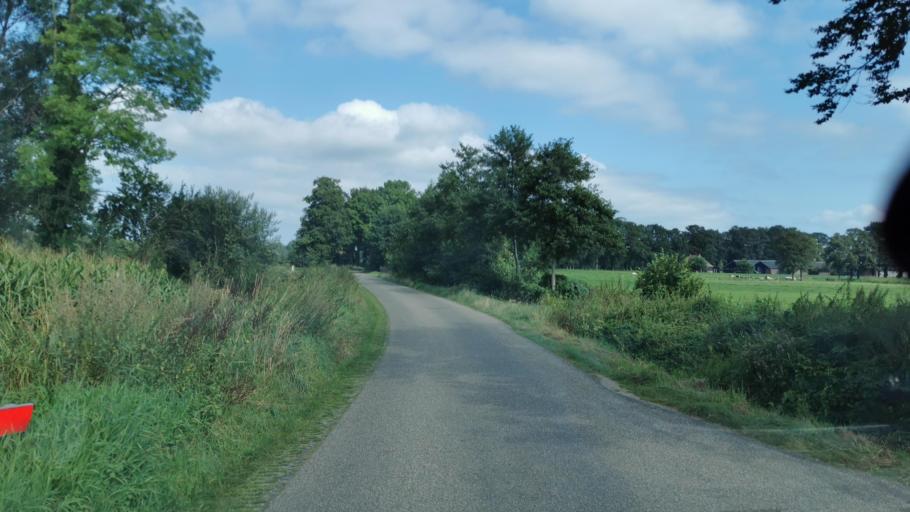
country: NL
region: Overijssel
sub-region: Gemeente Hengelo
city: Hengelo
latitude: 52.3318
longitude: 6.8441
